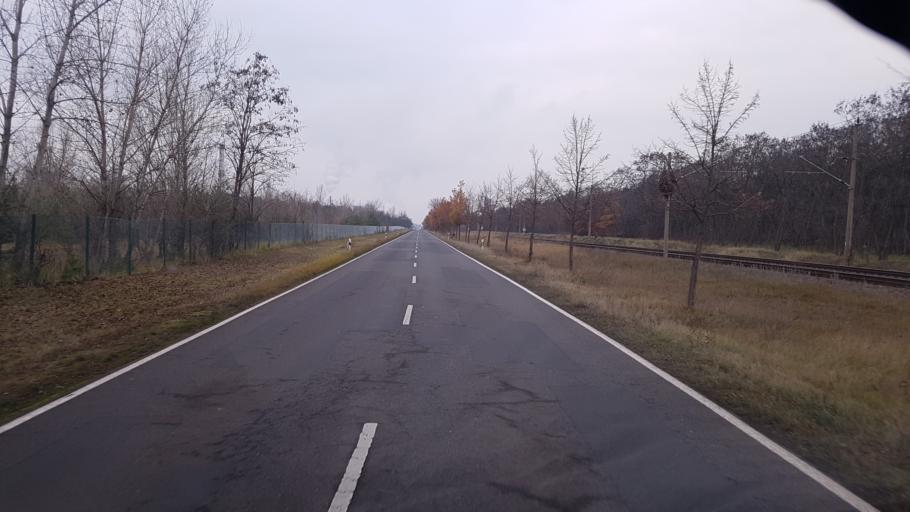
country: DE
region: Brandenburg
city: Eisenhuettenstadt
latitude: 52.1603
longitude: 14.6555
